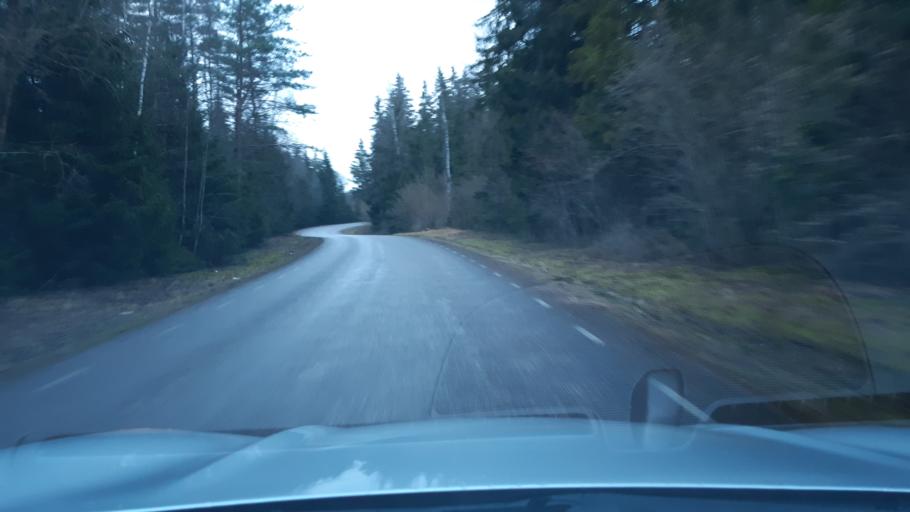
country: EE
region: Harju
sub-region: Saue linn
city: Saue
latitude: 59.2177
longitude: 24.5488
